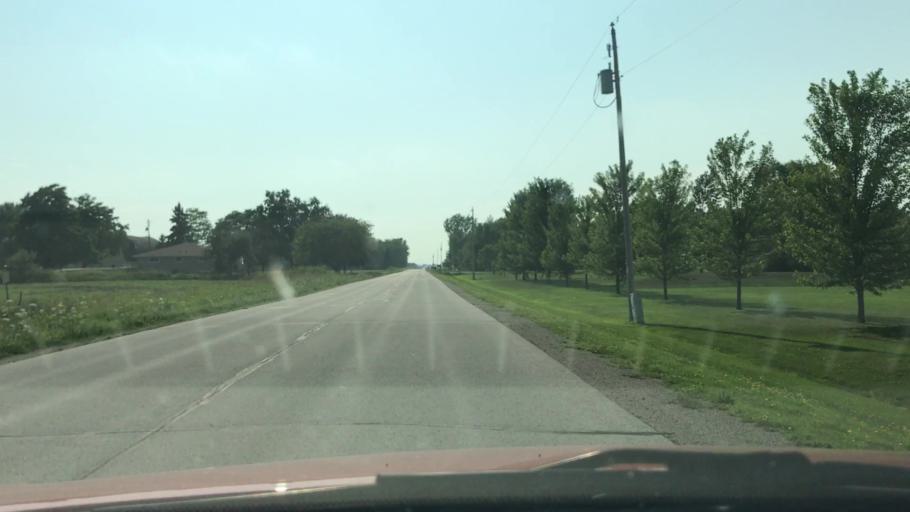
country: US
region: Wisconsin
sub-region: Brown County
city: Oneida
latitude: 44.4298
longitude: -88.1628
